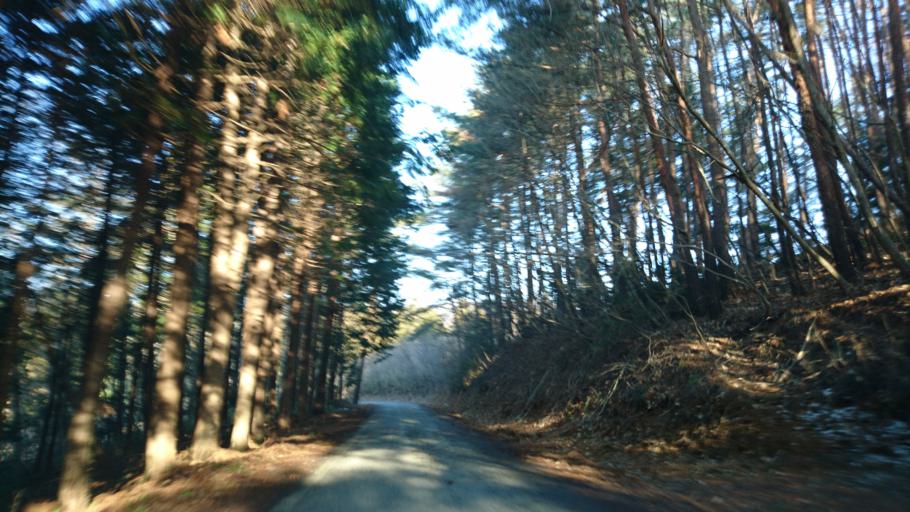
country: JP
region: Iwate
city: Ichinoseki
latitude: 38.9131
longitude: 141.2868
